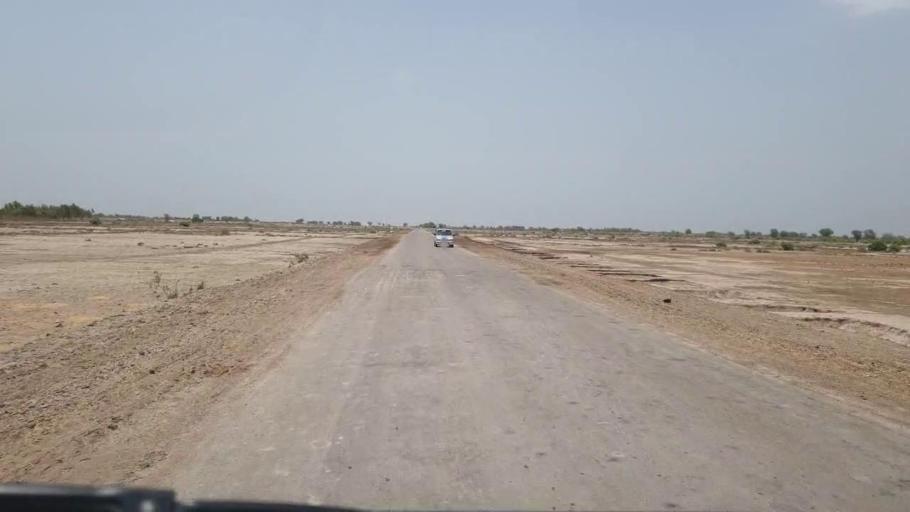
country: PK
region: Sindh
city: Daulatpur
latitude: 26.4491
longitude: 68.1168
